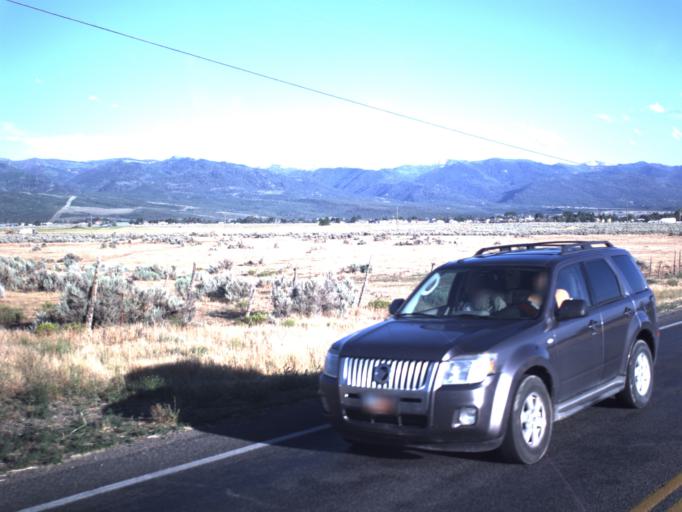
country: US
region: Utah
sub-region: Sanpete County
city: Mount Pleasant
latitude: 39.5642
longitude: -111.4555
